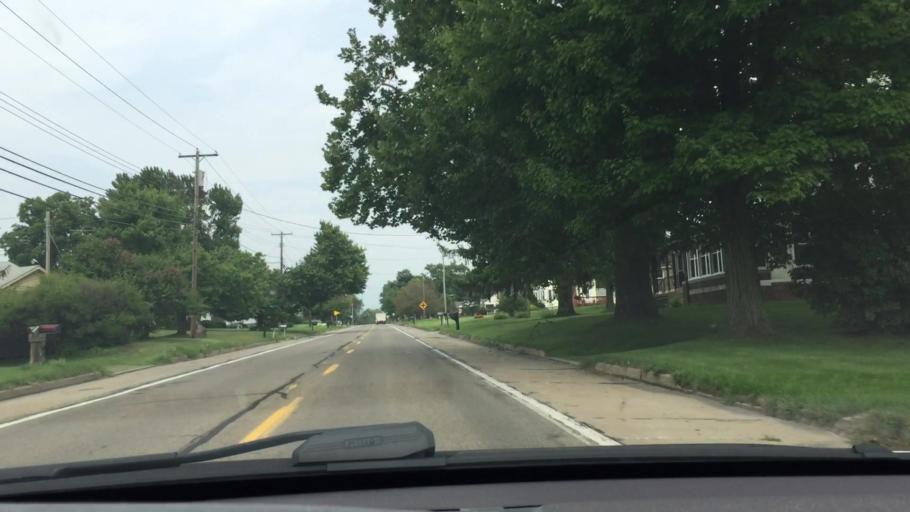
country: US
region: Pennsylvania
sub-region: Lawrence County
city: Oakland
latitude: 40.9681
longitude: -80.4121
